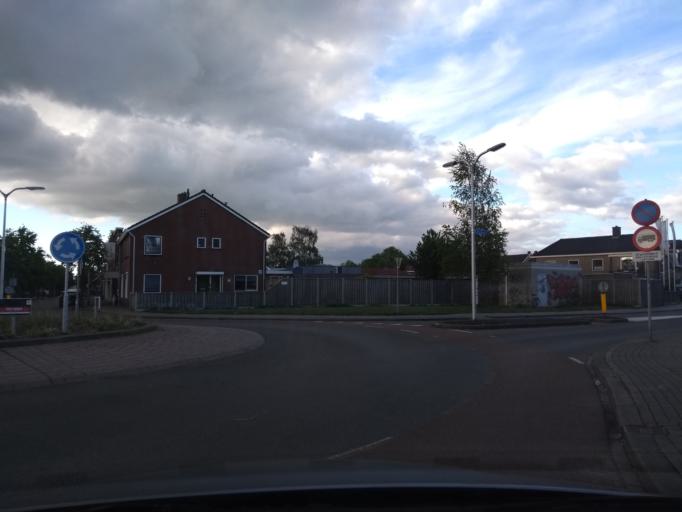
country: NL
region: Overijssel
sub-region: Gemeente Almelo
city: Almelo
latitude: 52.3408
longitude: 6.6615
